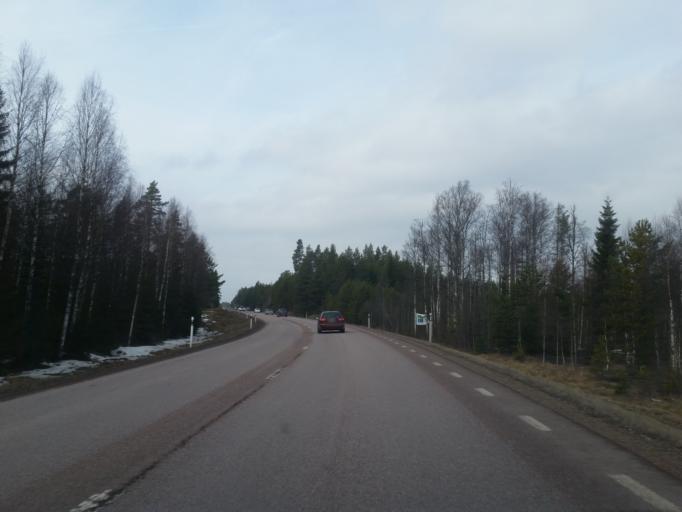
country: SE
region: Dalarna
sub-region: Mora Kommun
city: Mora
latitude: 60.9875
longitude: 14.6822
